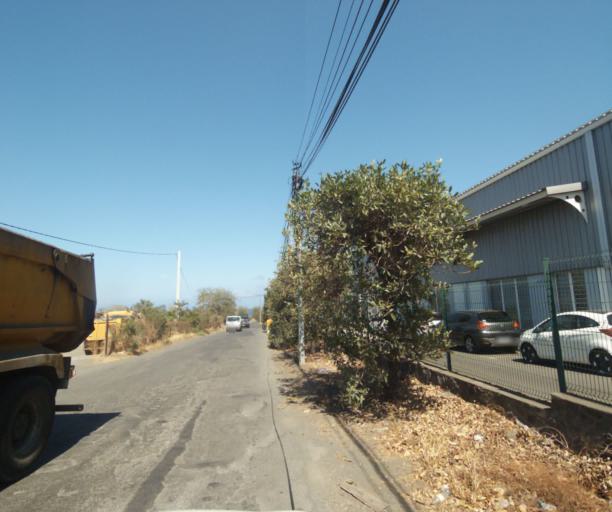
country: RE
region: Reunion
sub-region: Reunion
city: Le Port
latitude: -20.9631
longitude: 55.2915
